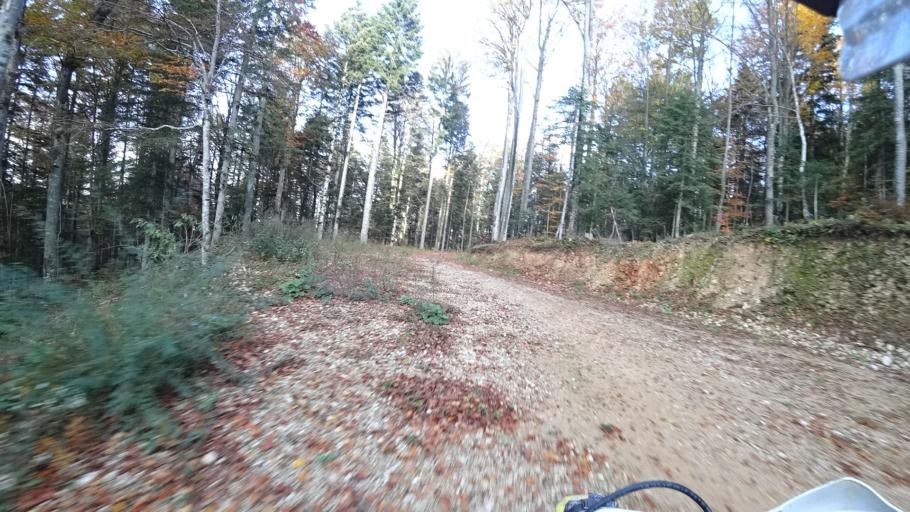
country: HR
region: Karlovacka
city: Plaski
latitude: 44.9657
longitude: 15.3905
